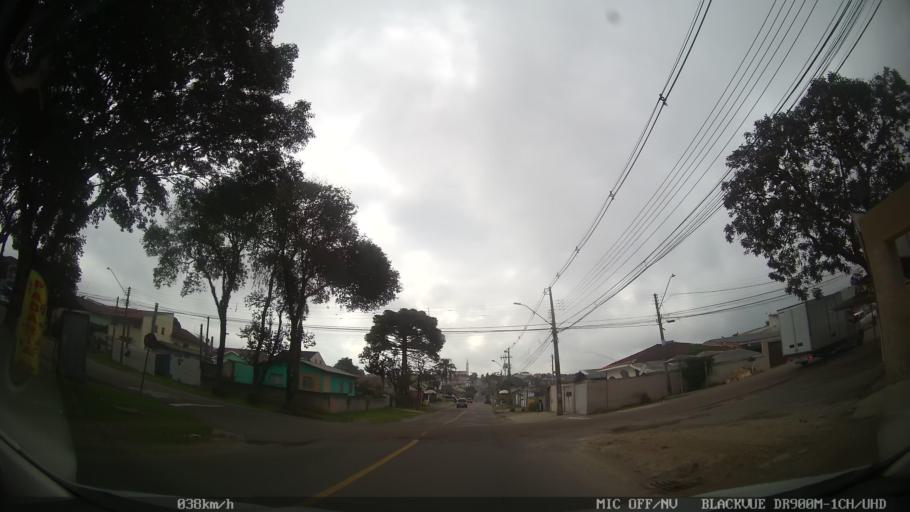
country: BR
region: Parana
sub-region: Curitiba
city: Curitiba
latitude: -25.3702
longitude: -49.2699
